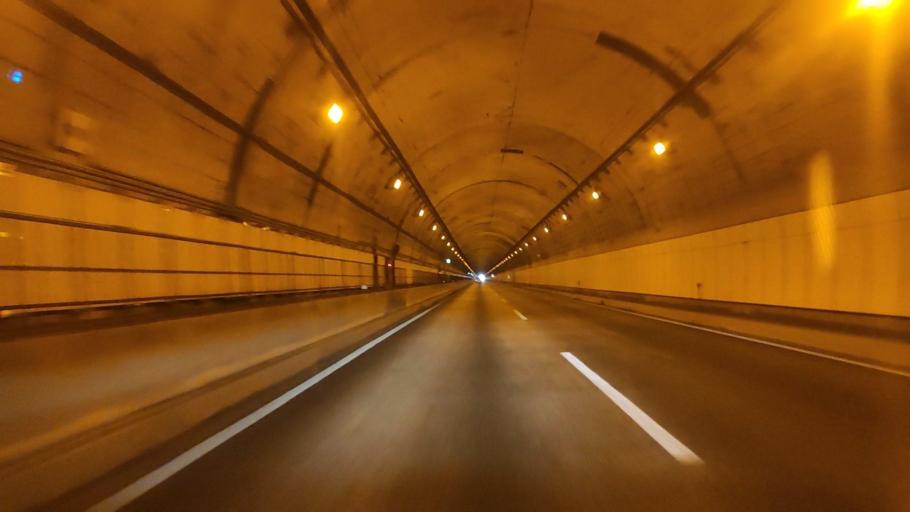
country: JP
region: Miyazaki
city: Miyakonojo
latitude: 31.8234
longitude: 131.2364
